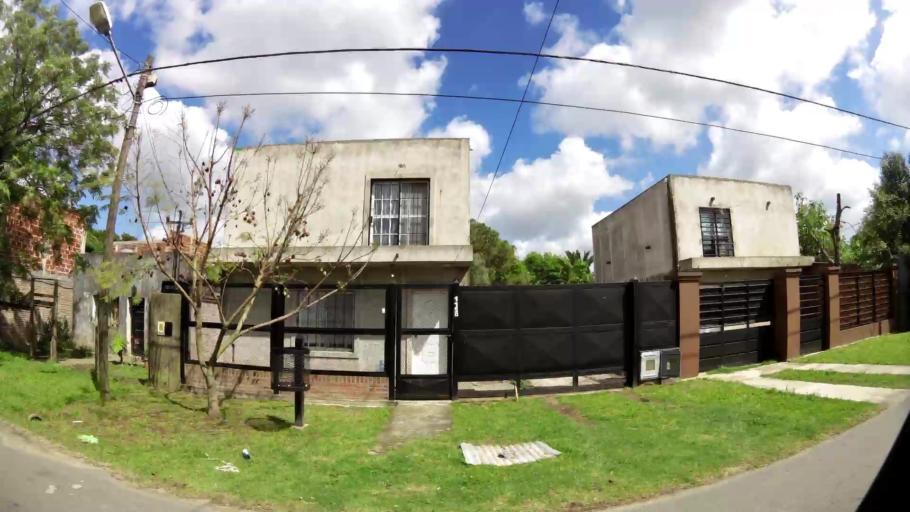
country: AR
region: Buenos Aires
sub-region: Partido de Quilmes
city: Quilmes
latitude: -34.8255
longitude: -58.1895
